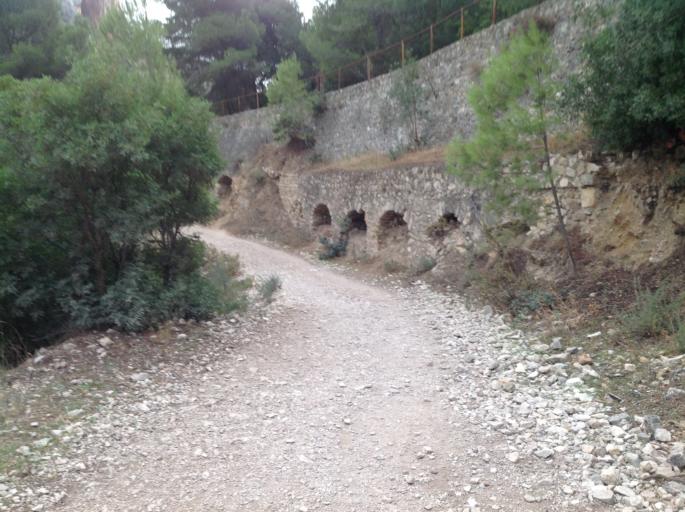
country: ES
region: Andalusia
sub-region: Provincia de Malaga
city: Carratraca
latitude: 36.9196
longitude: -4.7786
